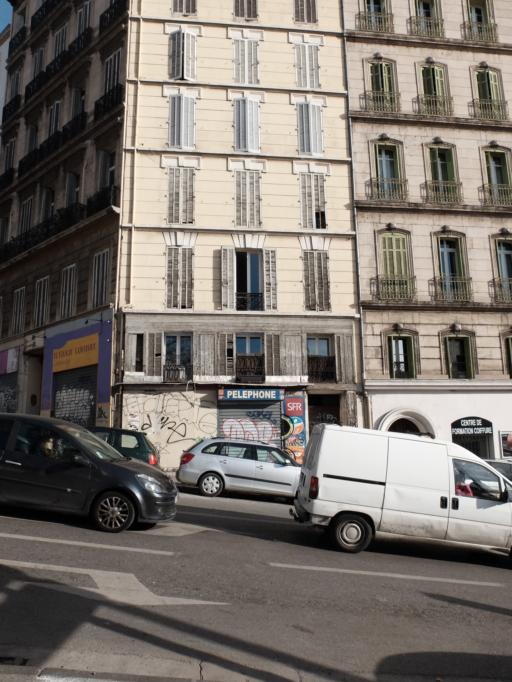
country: FR
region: Provence-Alpes-Cote d'Azur
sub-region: Departement des Bouches-du-Rhone
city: Marseille
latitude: 43.2919
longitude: 5.3831
